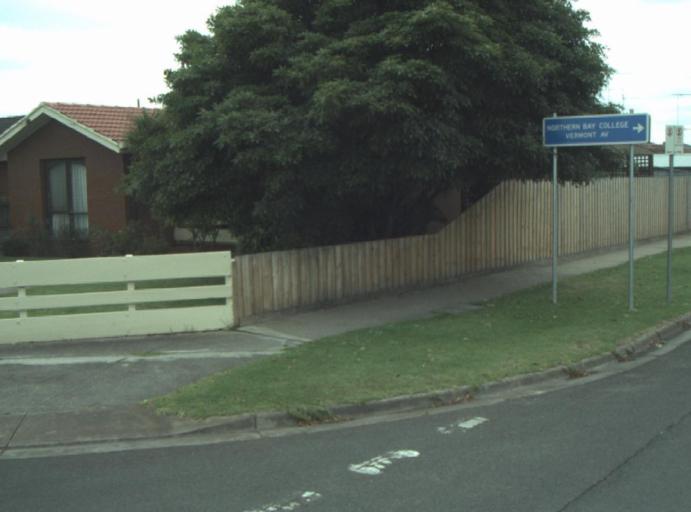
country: AU
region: Victoria
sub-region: Greater Geelong
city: Bell Park
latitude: -38.0809
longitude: 144.3469
